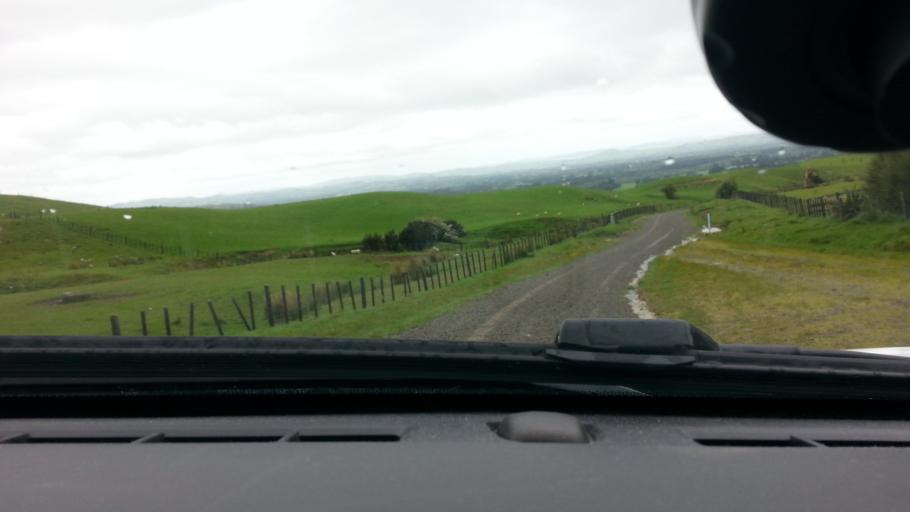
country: NZ
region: Wellington
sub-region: Masterton District
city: Masterton
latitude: -40.9230
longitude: 175.5379
